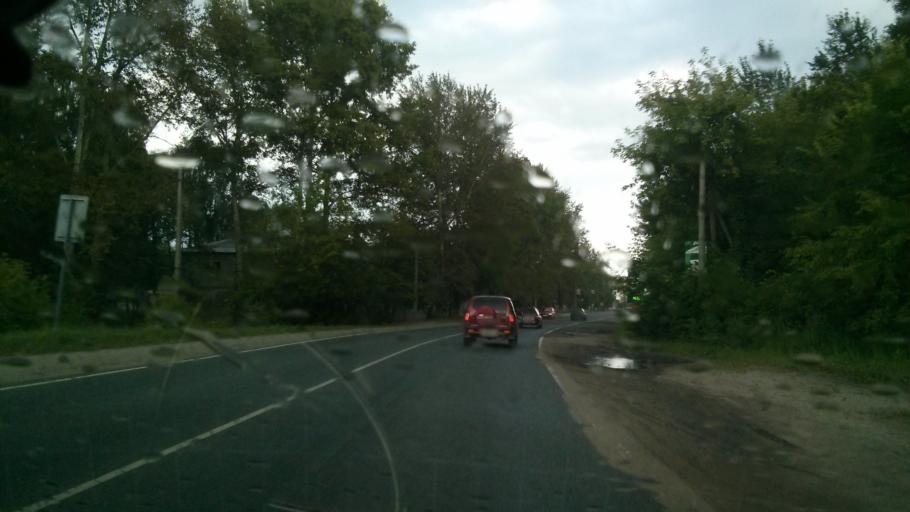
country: RU
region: Vladimir
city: Murom
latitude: 55.5975
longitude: 42.0333
